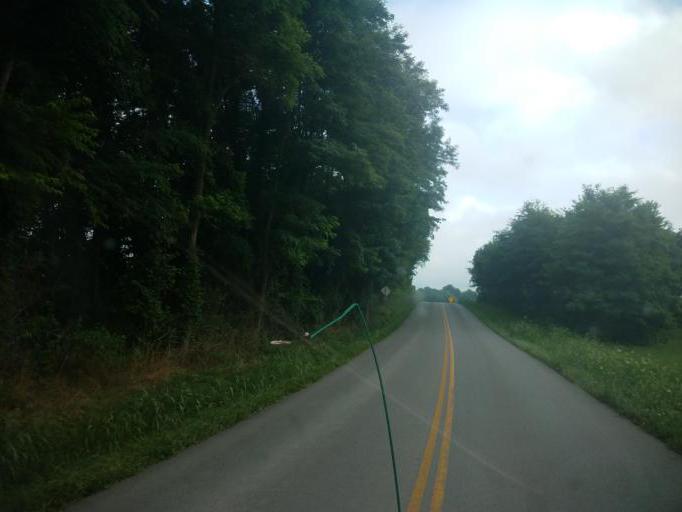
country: US
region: Kentucky
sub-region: Clinton County
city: Albany
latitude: 36.7571
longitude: -85.1369
